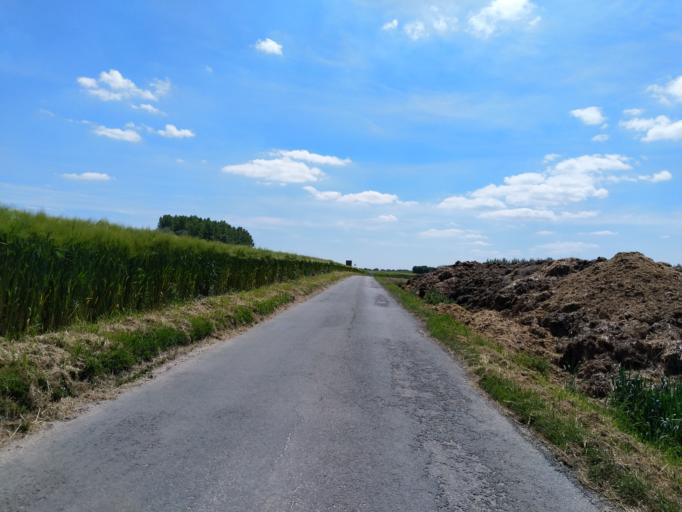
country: BE
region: Wallonia
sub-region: Province du Hainaut
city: Roeulx
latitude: 50.5051
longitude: 4.0420
